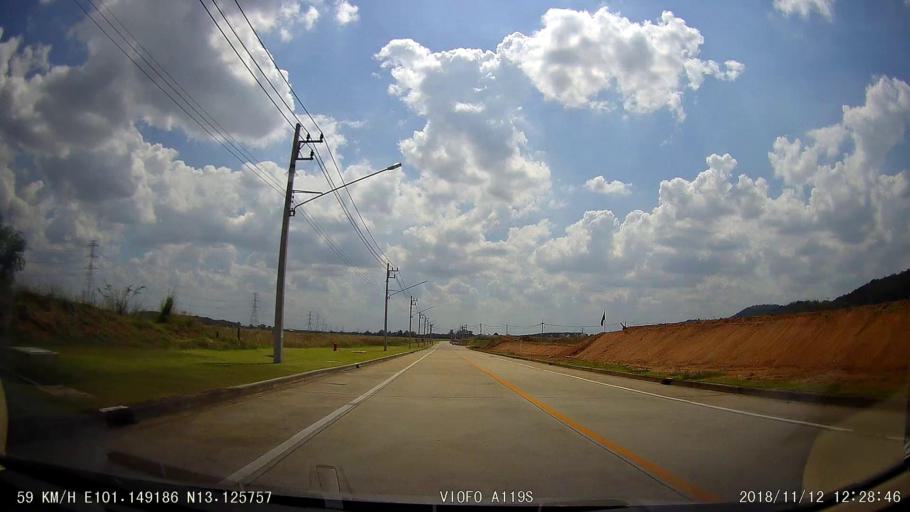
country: TH
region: Chon Buri
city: Ban Talat Bueng
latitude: 13.1254
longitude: 101.1492
